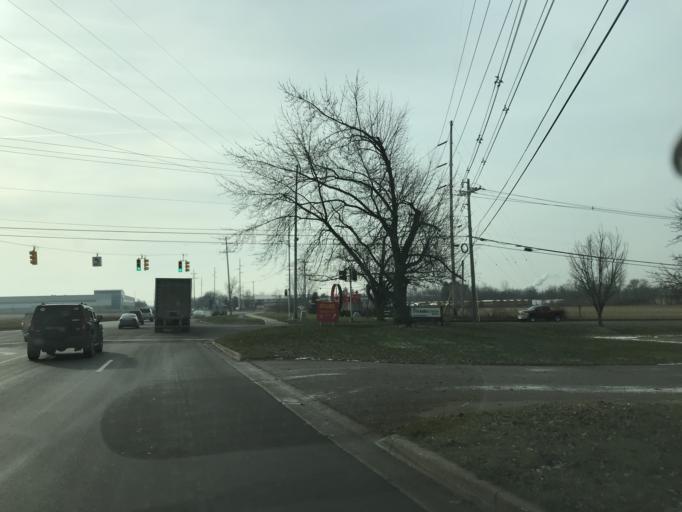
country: US
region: Michigan
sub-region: Ottawa County
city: Holland
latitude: 42.7693
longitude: -86.0774
